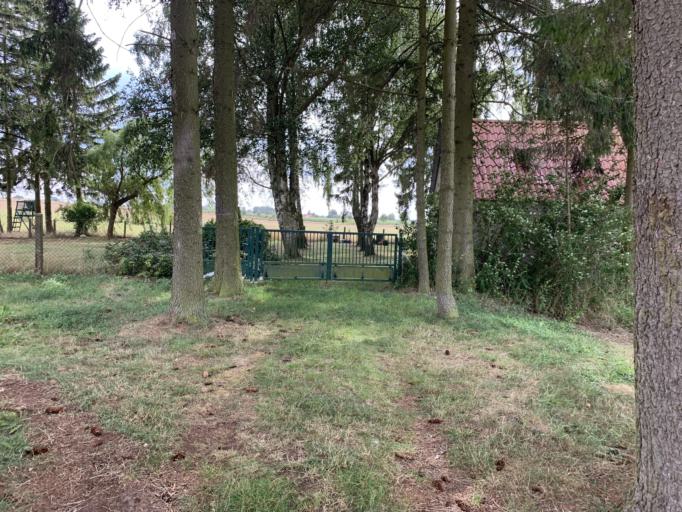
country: DE
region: Mecklenburg-Vorpommern
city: Blankensee
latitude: 53.3990
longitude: 13.2916
